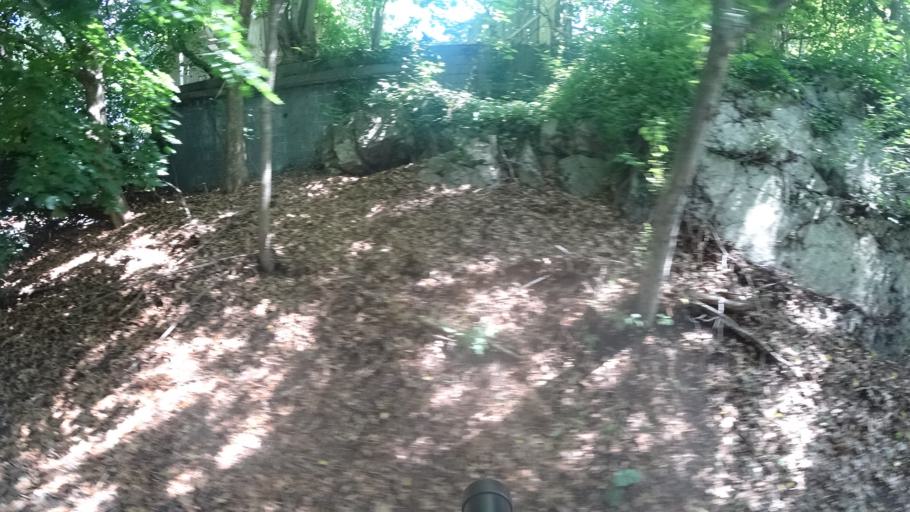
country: US
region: Massachusetts
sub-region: Norfolk County
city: Dedham
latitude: 42.2544
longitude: -71.1576
